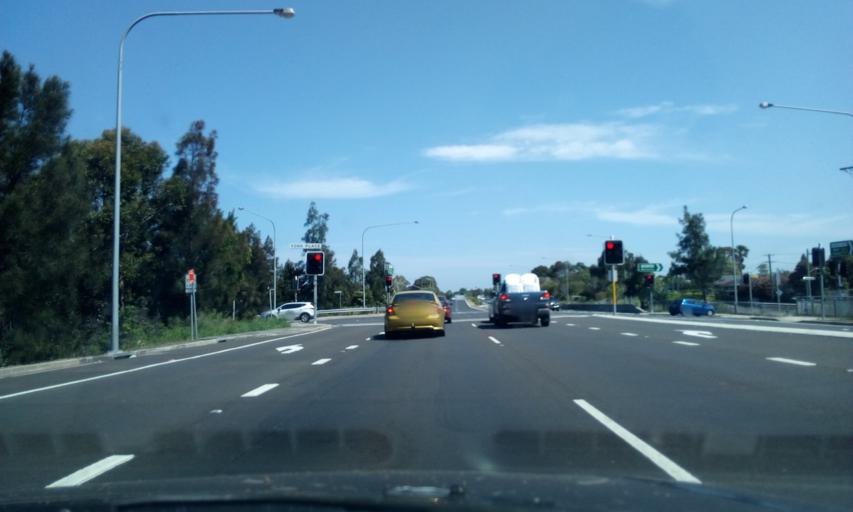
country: AU
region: New South Wales
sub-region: Wollongong
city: Bulli
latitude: -34.3539
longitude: 150.9103
